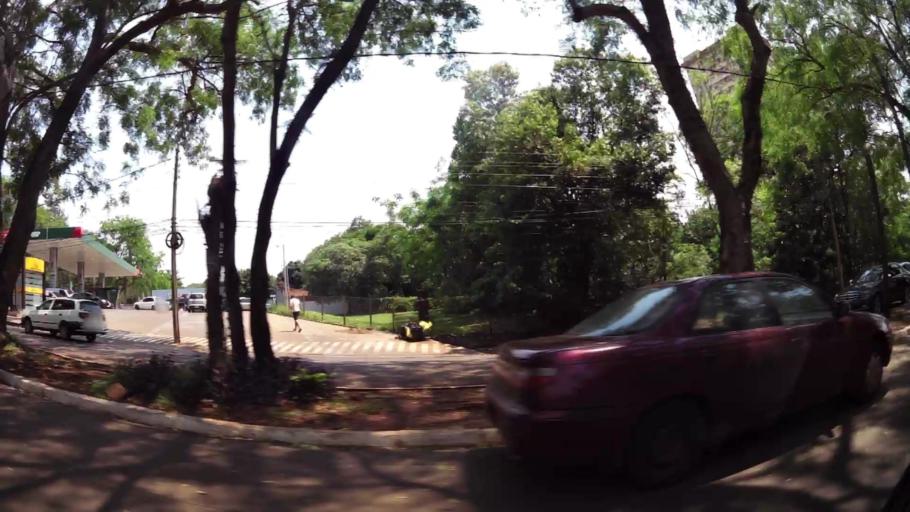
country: PY
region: Alto Parana
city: Ciudad del Este
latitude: -25.5186
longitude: -54.6112
